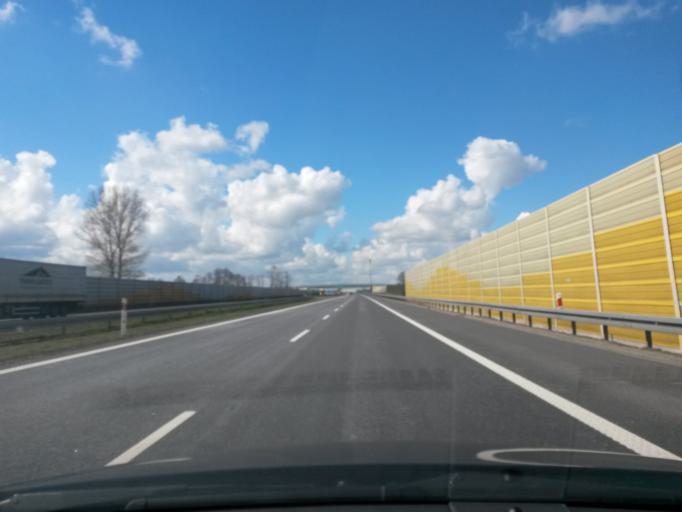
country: PL
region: Lodz Voivodeship
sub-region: Powiat poddebicki
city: Wartkowice
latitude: 52.0079
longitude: 18.9781
